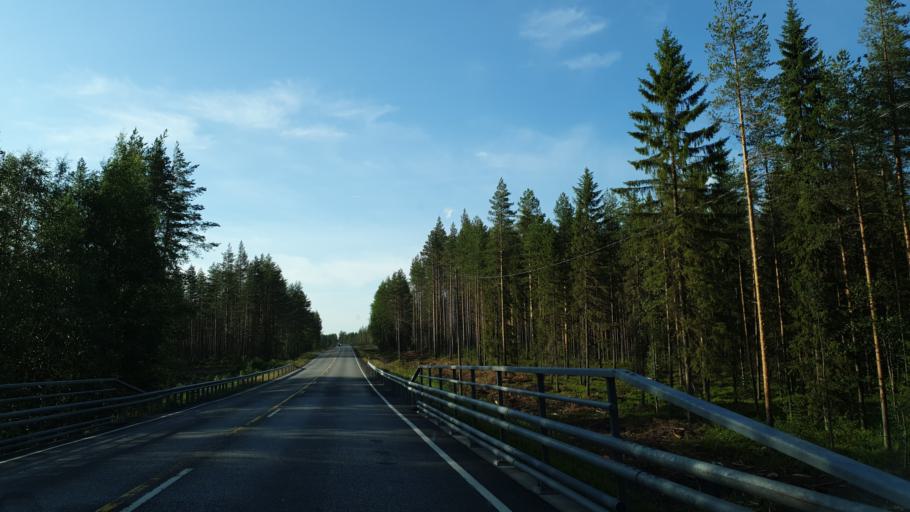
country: FI
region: Kainuu
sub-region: Kehys-Kainuu
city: Kuhmo
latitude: 64.0867
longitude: 29.4829
